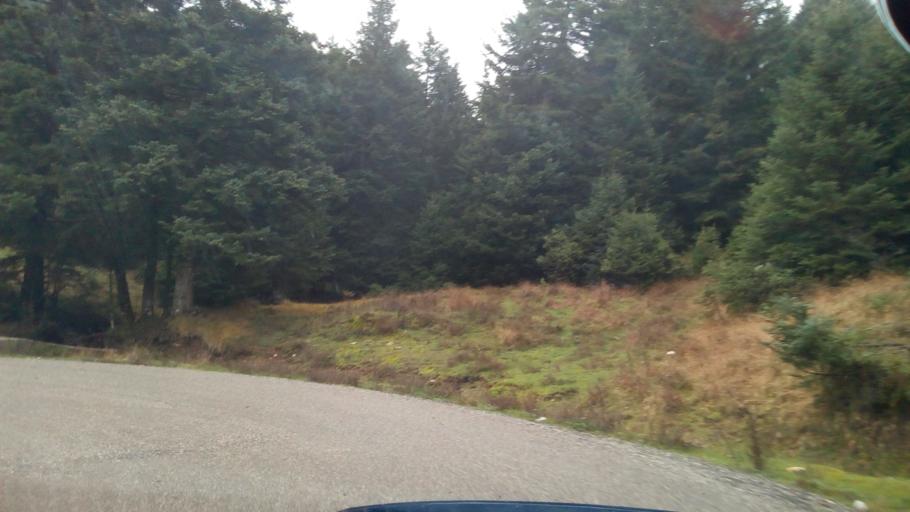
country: GR
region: West Greece
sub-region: Nomos Aitolias kai Akarnanias
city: Nafpaktos
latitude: 38.5360
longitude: 21.8575
